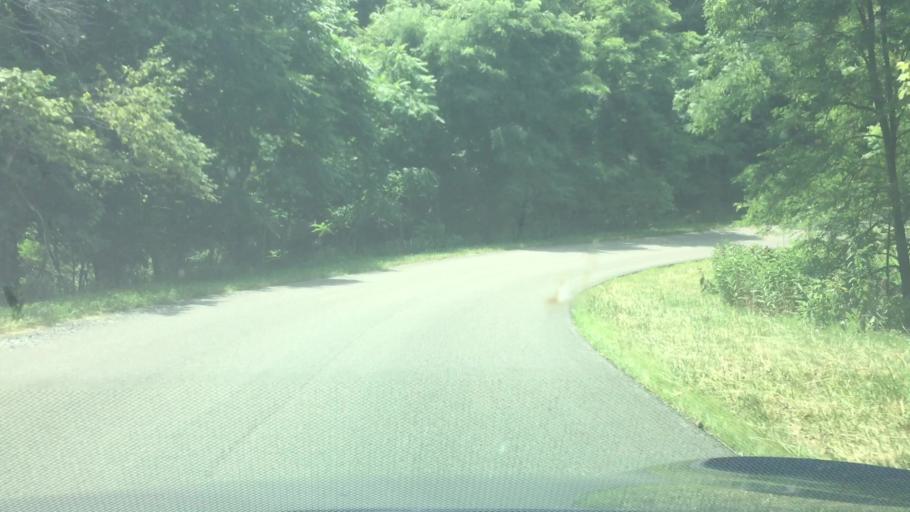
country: US
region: Virginia
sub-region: Wythe County
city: Wytheville
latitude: 36.9245
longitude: -81.0554
